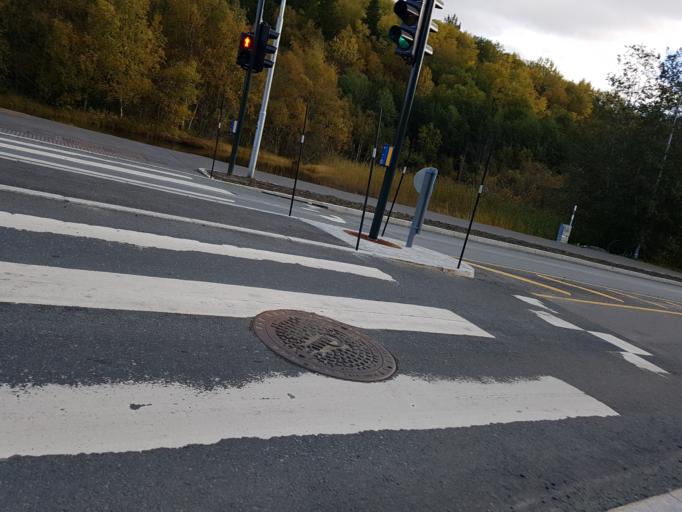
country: NO
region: Sor-Trondelag
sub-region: Klaebu
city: Klaebu
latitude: 63.4022
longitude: 10.5092
